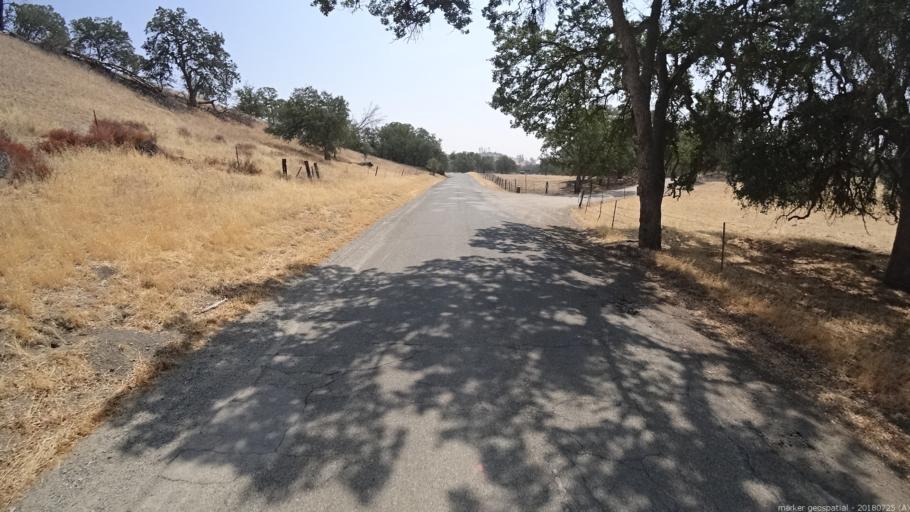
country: US
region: California
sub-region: San Luis Obispo County
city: Shandon
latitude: 35.8750
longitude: -120.4140
